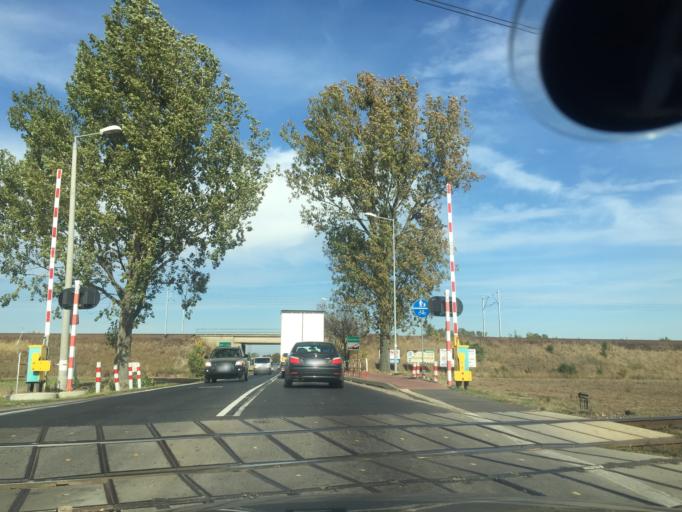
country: PL
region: Greater Poland Voivodeship
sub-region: Powiat wrzesinski
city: Wrzesnia
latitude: 52.3384
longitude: 17.5637
